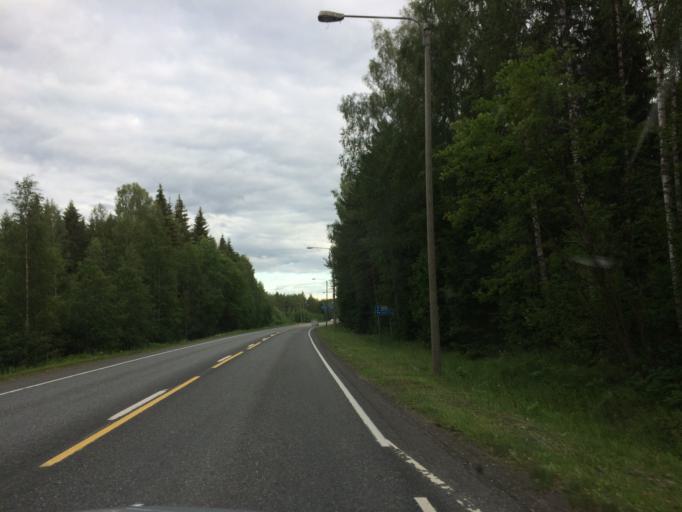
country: FI
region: Haeme
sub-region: Haemeenlinna
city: Haemeenlinna
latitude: 60.9442
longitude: 24.5163
